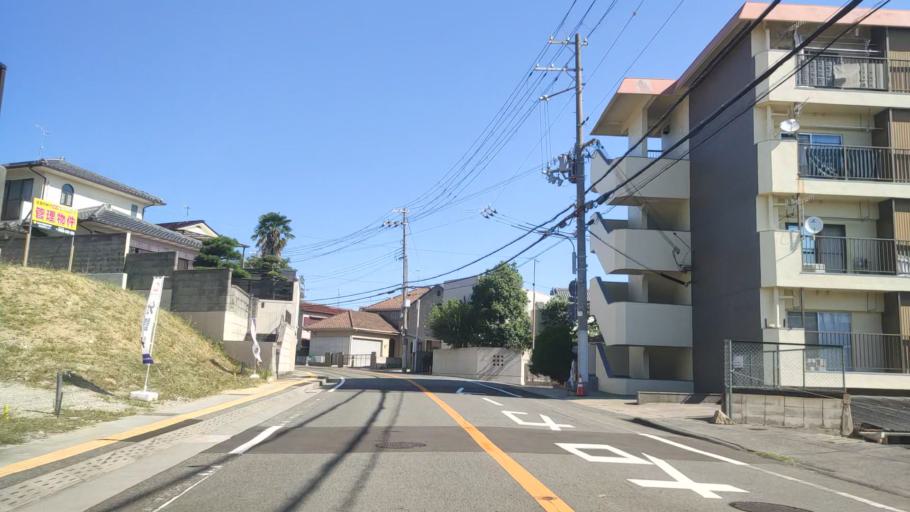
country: JP
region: Hyogo
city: Akashi
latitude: 34.6518
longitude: 135.0031
